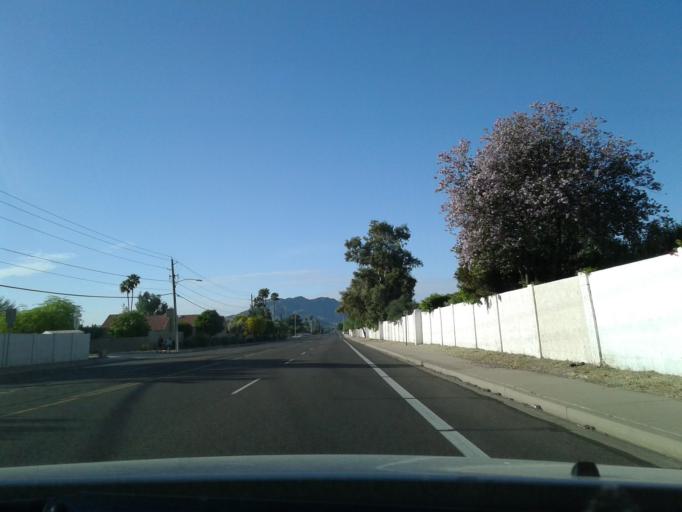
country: US
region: Arizona
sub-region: Maricopa County
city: Paradise Valley
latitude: 33.6024
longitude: -111.9959
